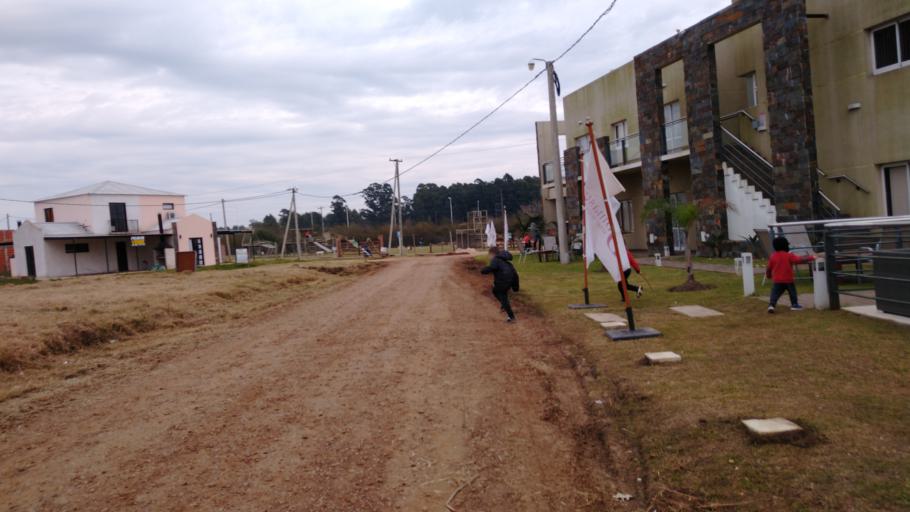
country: AR
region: Entre Rios
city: Chajari
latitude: -30.7418
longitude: -58.0129
